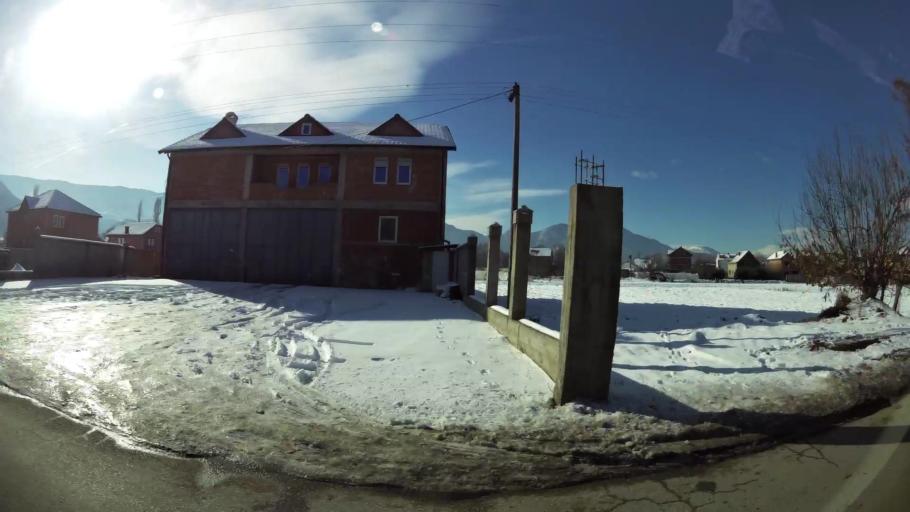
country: MK
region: Saraj
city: Saraj
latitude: 41.9999
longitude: 21.3393
